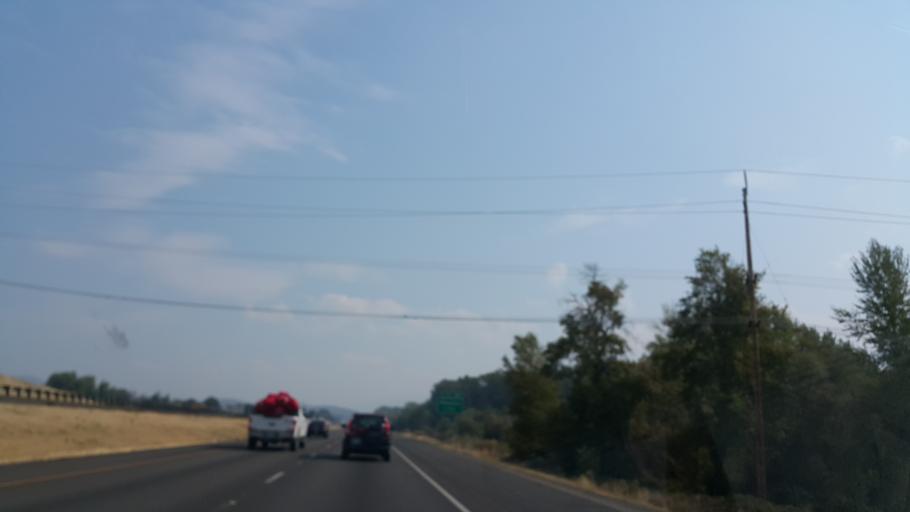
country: US
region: Oregon
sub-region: Jackson County
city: Phoenix
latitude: 42.2964
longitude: -122.8322
